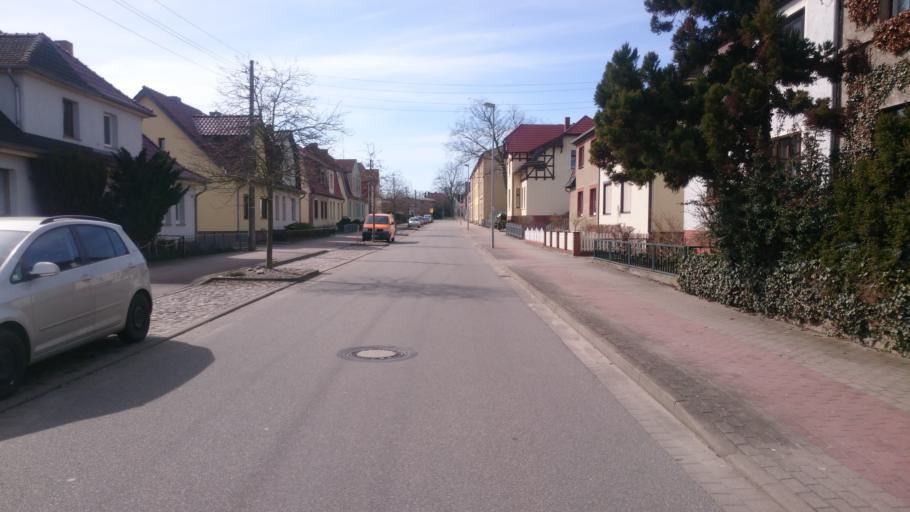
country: DE
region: Mecklenburg-Vorpommern
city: Teterow
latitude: 53.7802
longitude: 12.5734
